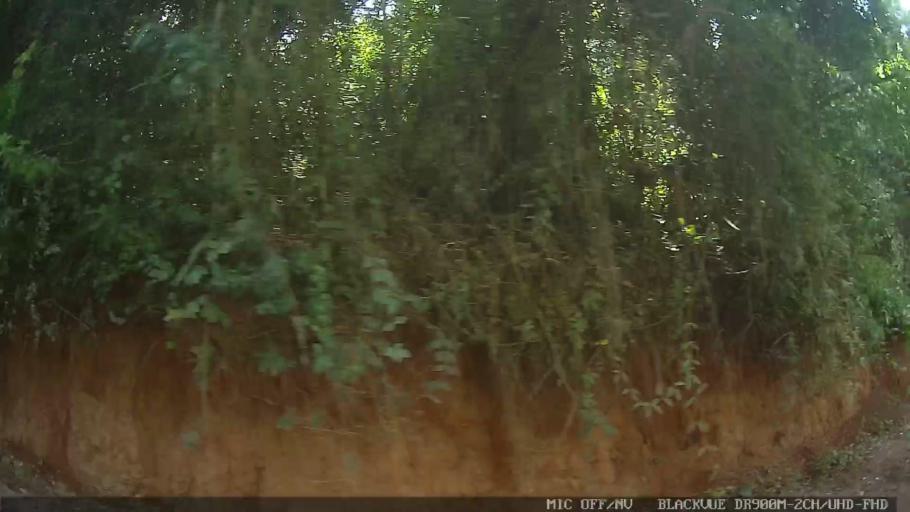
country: BR
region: Sao Paulo
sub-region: Jarinu
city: Jarinu
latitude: -22.9977
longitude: -46.6620
